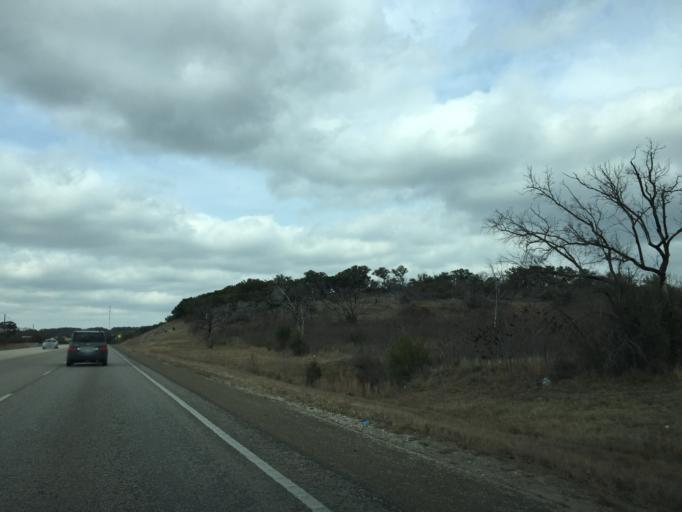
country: US
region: Texas
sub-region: Travis County
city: Briarcliff
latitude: 30.4207
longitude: -98.1259
